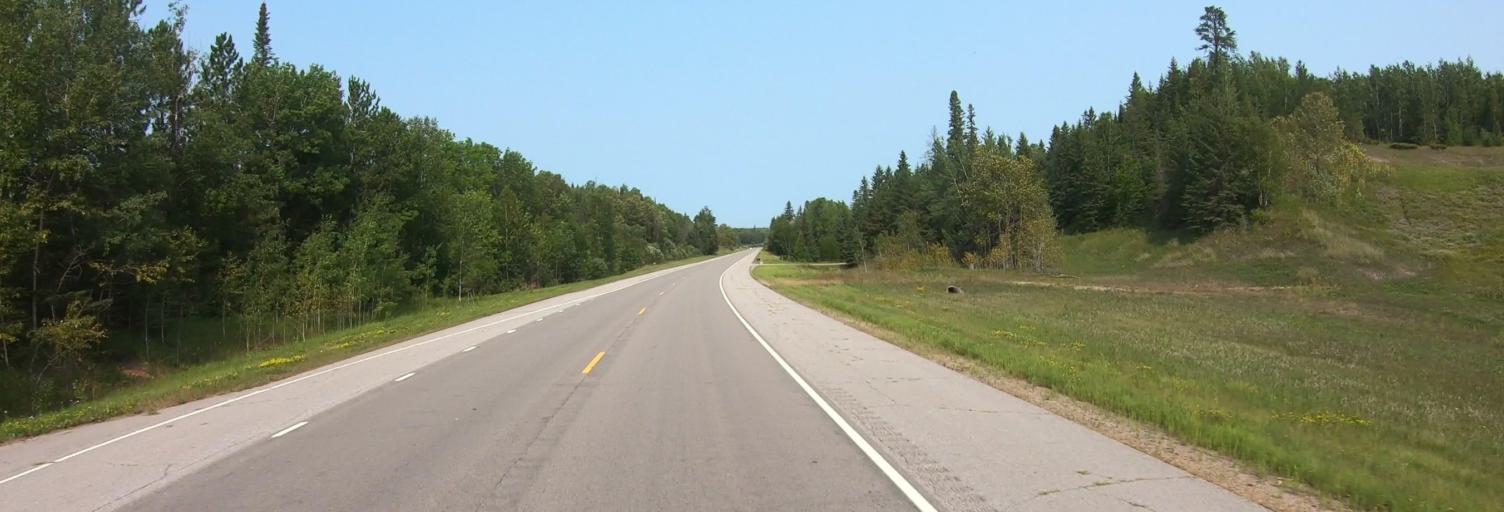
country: CA
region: Ontario
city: Fort Frances
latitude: 48.2223
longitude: -92.9209
